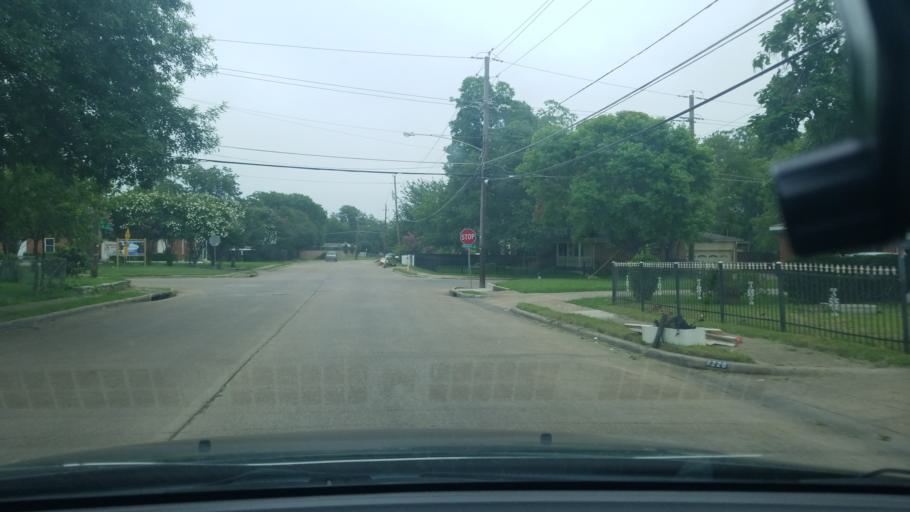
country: US
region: Texas
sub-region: Dallas County
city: Balch Springs
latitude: 32.7550
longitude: -96.6791
